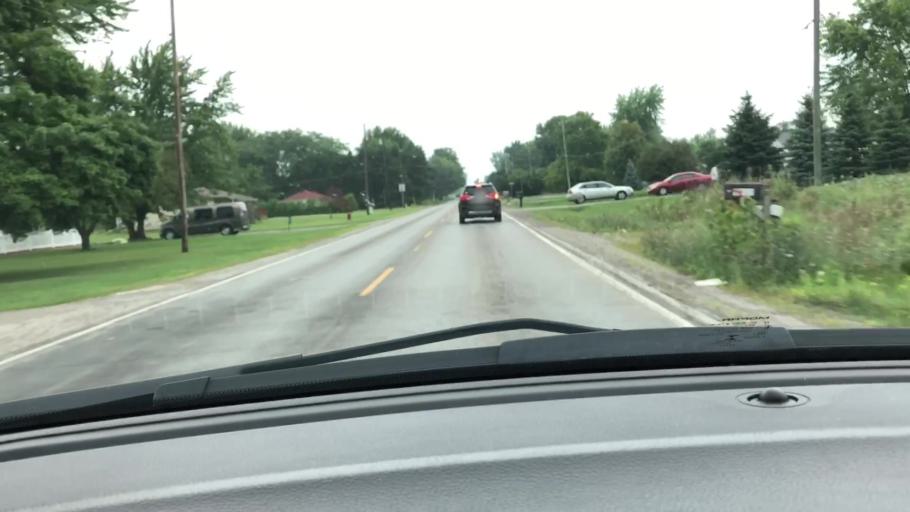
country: US
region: Michigan
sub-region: Saginaw County
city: Freeland
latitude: 43.4945
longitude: -84.0912
